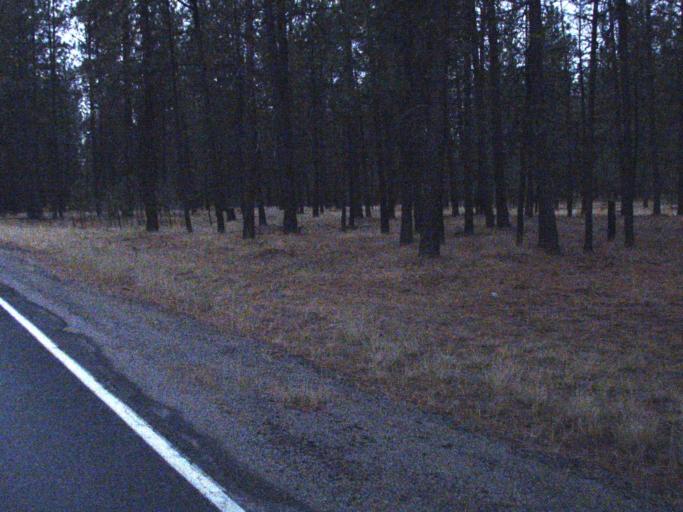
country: US
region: Washington
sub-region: Spokane County
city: Fairchild Air Force Base
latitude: 47.8548
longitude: -117.8475
